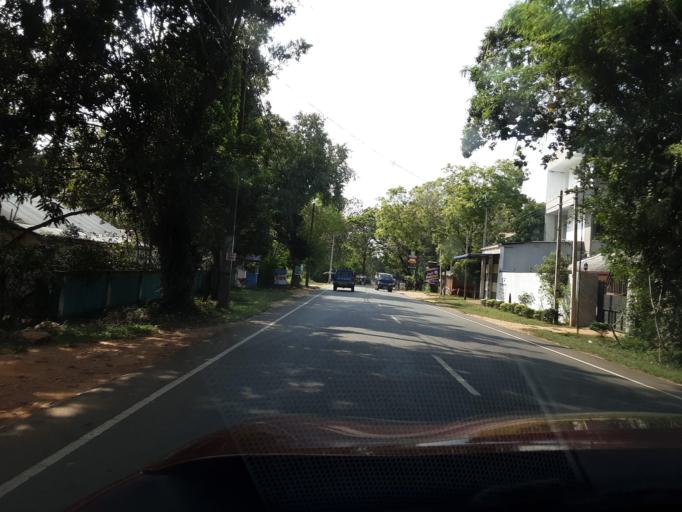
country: LK
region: Uva
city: Haputale
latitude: 6.3521
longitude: 81.1938
